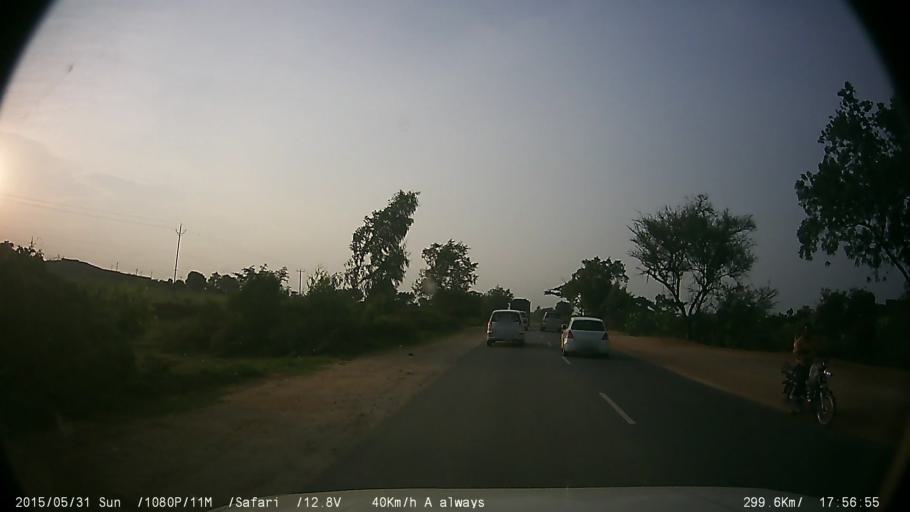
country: IN
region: Karnataka
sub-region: Mysore
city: Nanjangud
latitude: 11.9974
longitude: 76.6695
